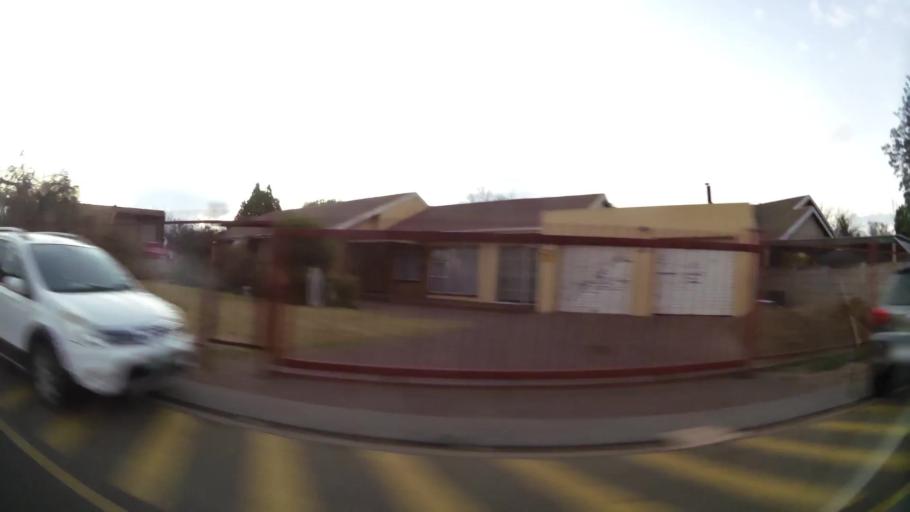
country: ZA
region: Orange Free State
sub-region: Mangaung Metropolitan Municipality
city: Bloemfontein
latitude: -29.1665
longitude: 26.1986
